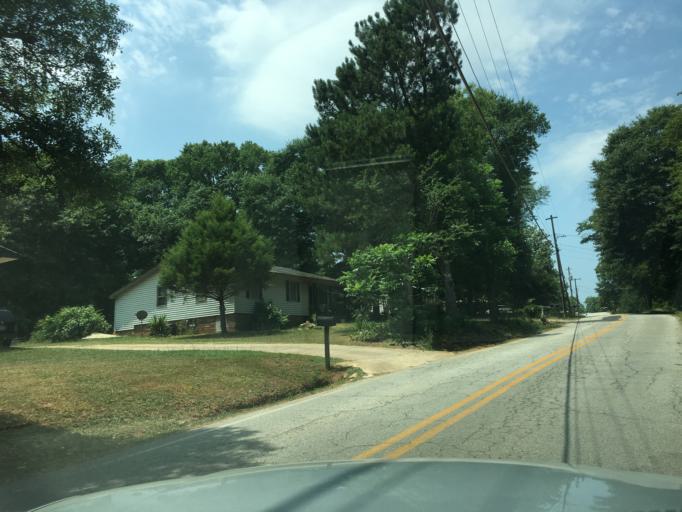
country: US
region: Georgia
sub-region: Hart County
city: Hartwell
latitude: 34.3448
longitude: -82.9348
